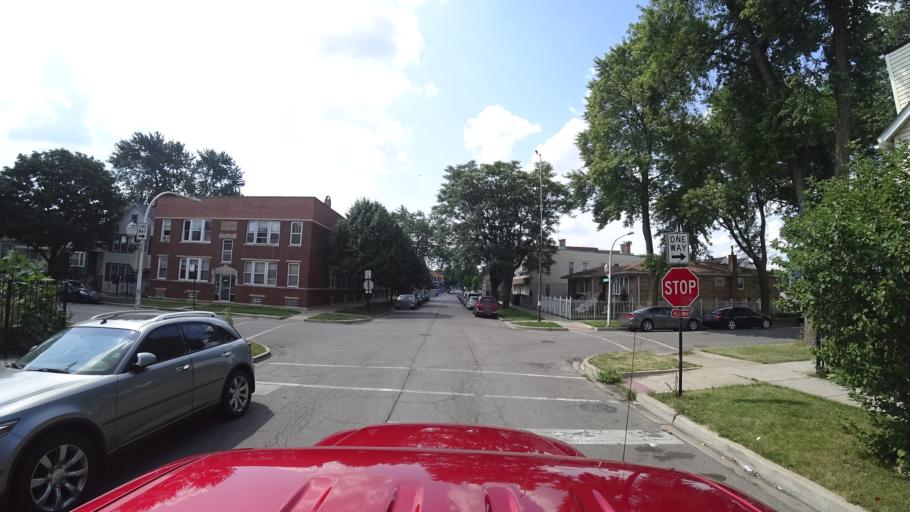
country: US
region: Illinois
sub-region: Cook County
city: Chicago
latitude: 41.8238
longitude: -87.6996
